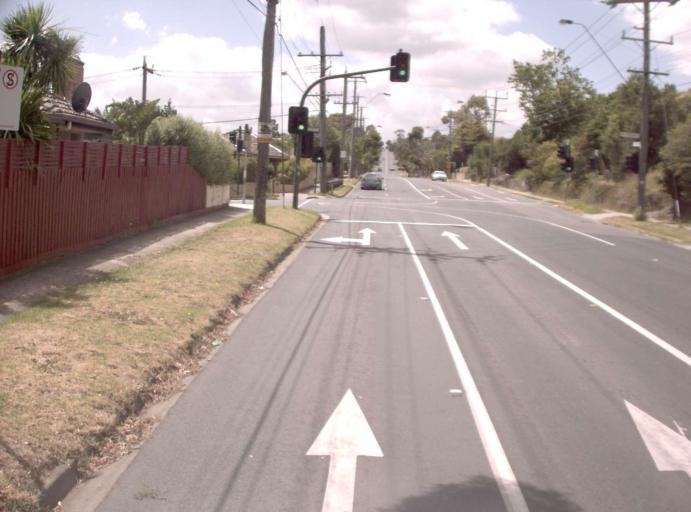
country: AU
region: Victoria
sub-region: Whitehorse
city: Burwood
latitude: -37.8560
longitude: 145.1184
